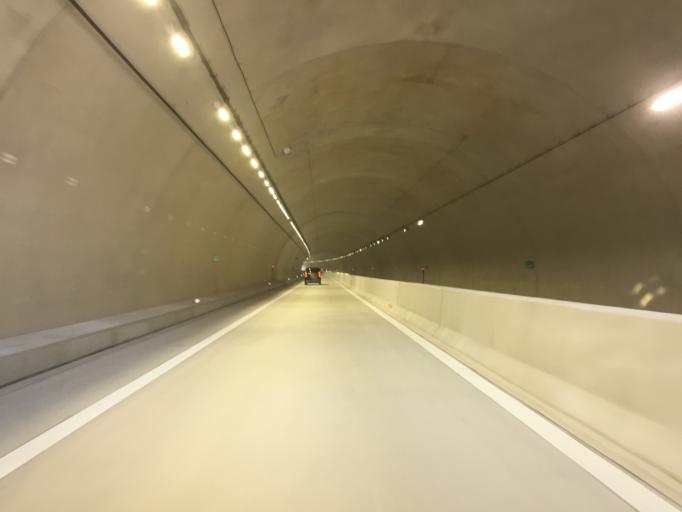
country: JP
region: Fukushima
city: Hobaramachi
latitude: 37.7560
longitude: 140.6203
